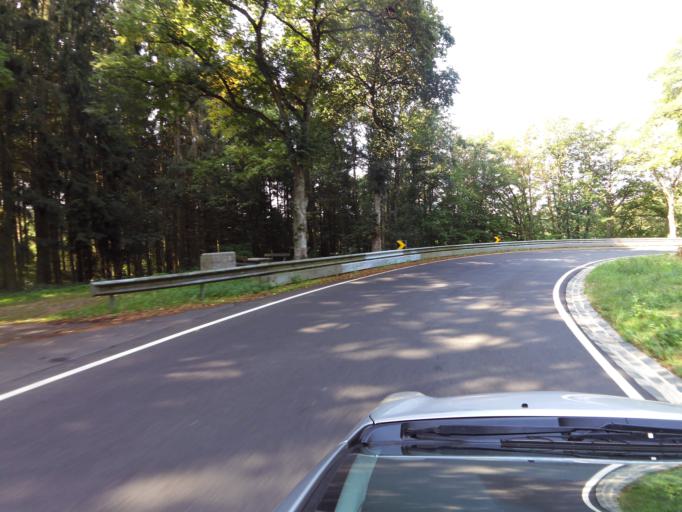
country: LU
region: Diekirch
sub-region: Canton de Wiltz
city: Goesdorf
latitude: 49.9106
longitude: 5.9821
